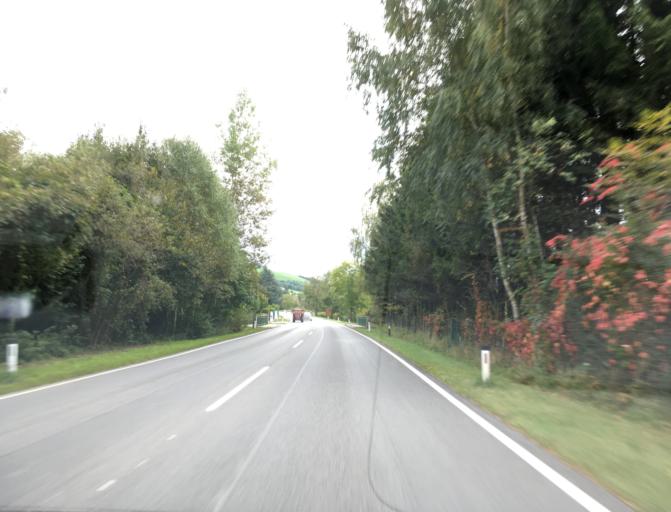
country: AT
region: Lower Austria
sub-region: Politischer Bezirk Neunkirchen
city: Thomasberg
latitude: 47.5291
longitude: 16.1814
